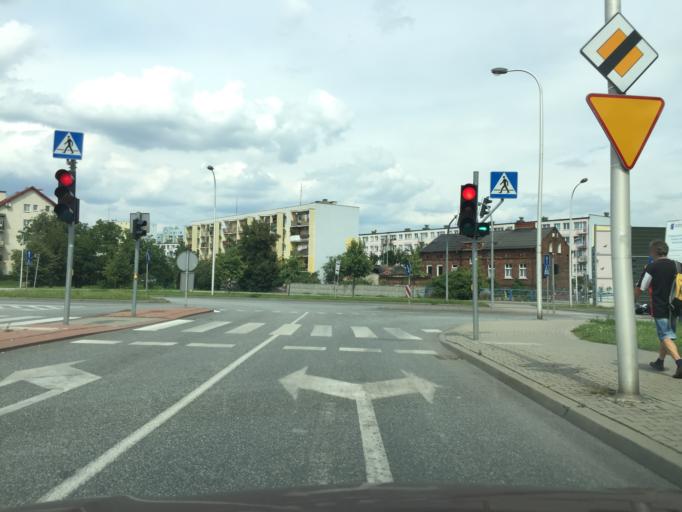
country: PL
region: Greater Poland Voivodeship
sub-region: Kalisz
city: Kalisz
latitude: 51.7444
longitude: 18.0730
